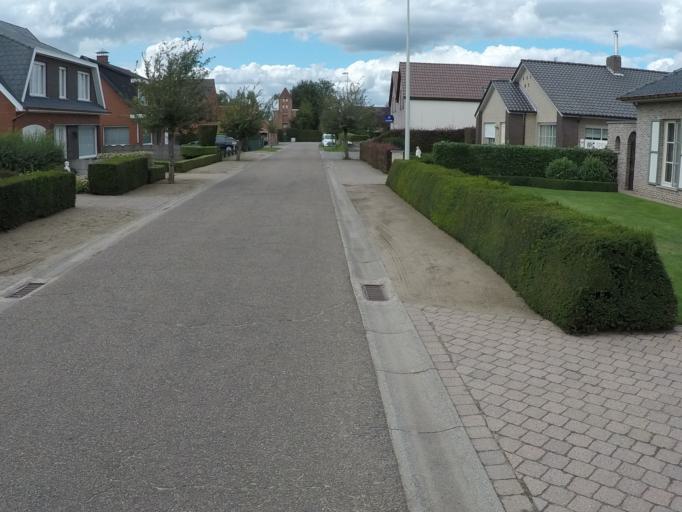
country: BE
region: Flanders
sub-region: Provincie Antwerpen
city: Zandhoven
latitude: 51.2233
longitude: 4.6975
